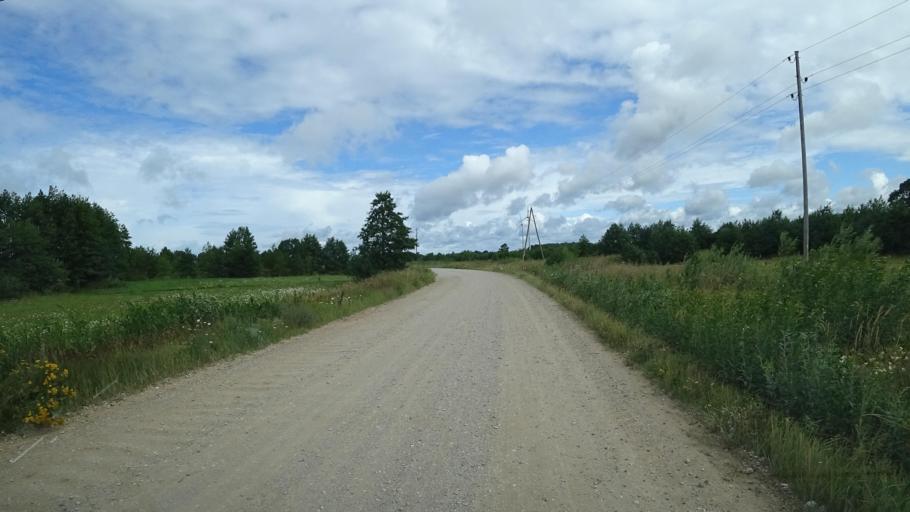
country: LV
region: Liepaja
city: Vec-Liepaja
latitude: 56.6280
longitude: 21.0485
